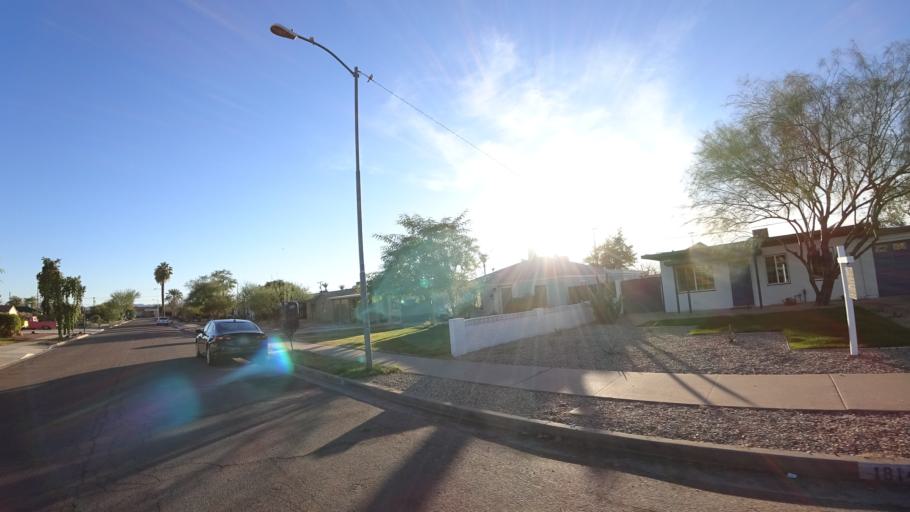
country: US
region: Arizona
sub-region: Maricopa County
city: Phoenix
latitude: 33.4683
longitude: -112.0950
